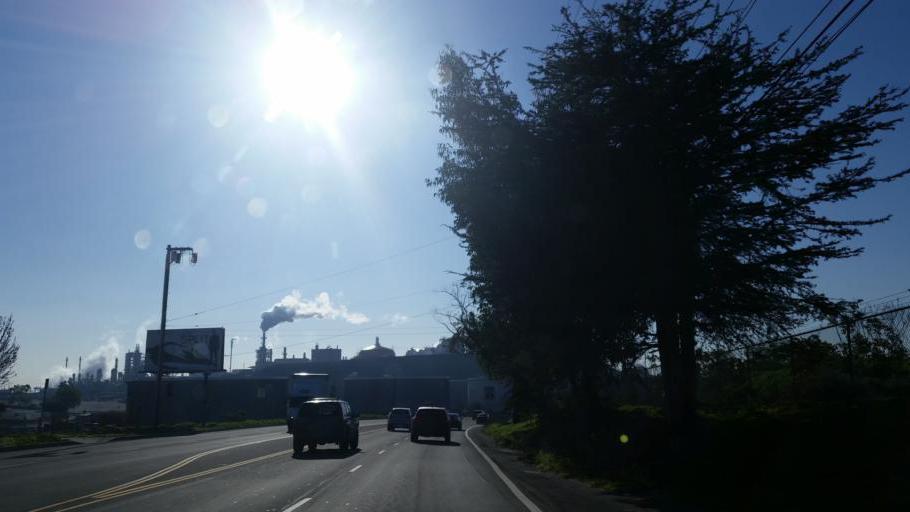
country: US
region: California
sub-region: Los Angeles County
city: Lomita
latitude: 33.7811
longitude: -118.2970
